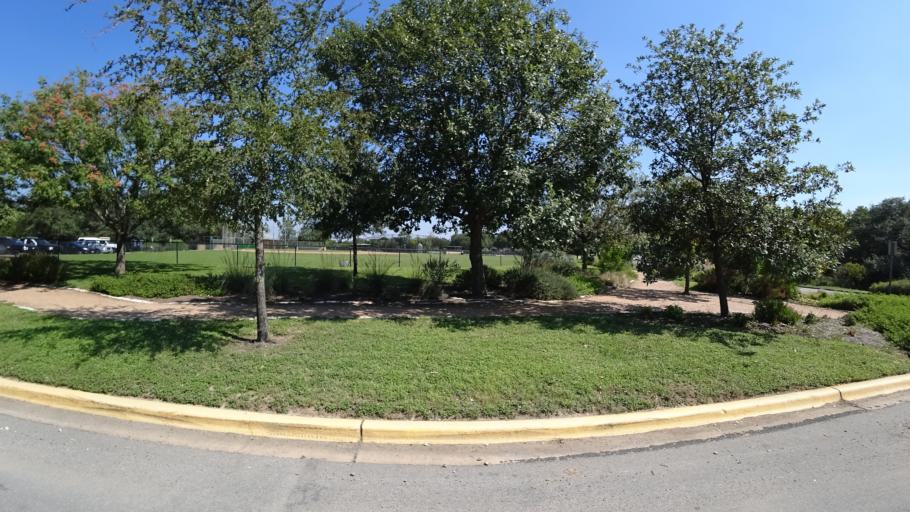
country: US
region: Texas
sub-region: Travis County
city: Rollingwood
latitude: 30.2747
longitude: -97.7884
